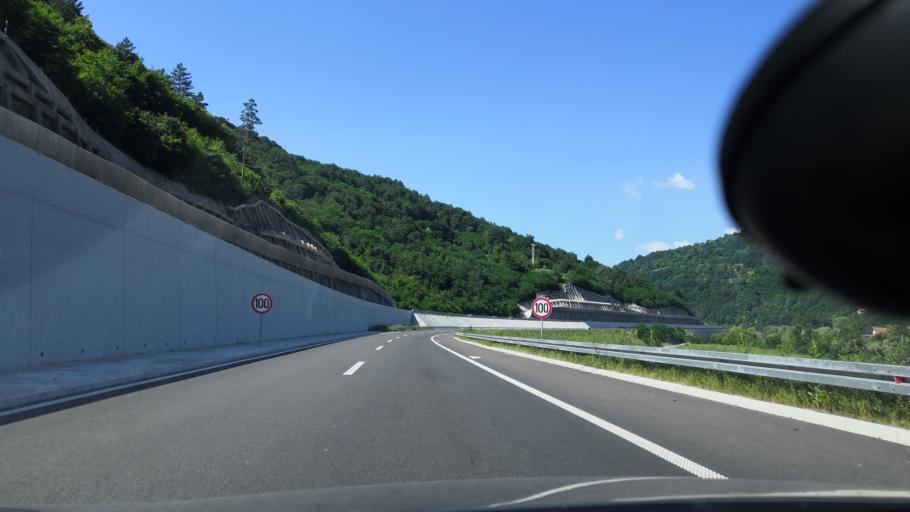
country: RS
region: Central Serbia
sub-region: Pcinjski Okrug
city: Vladicin Han
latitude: 42.7721
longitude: 22.0858
